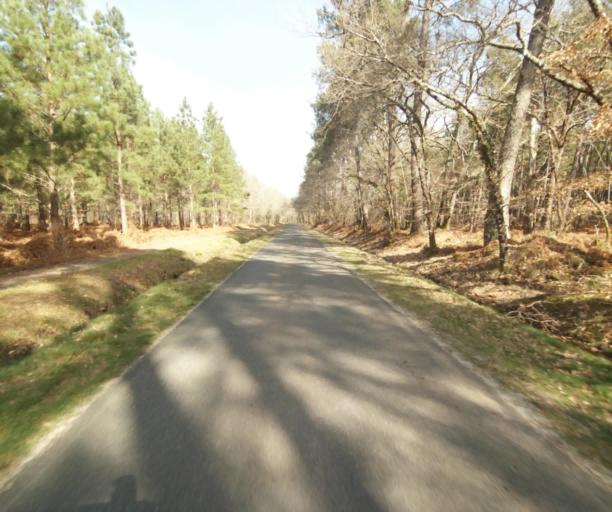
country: FR
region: Aquitaine
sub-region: Departement de la Gironde
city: Bazas
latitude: 44.2351
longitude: -0.2017
